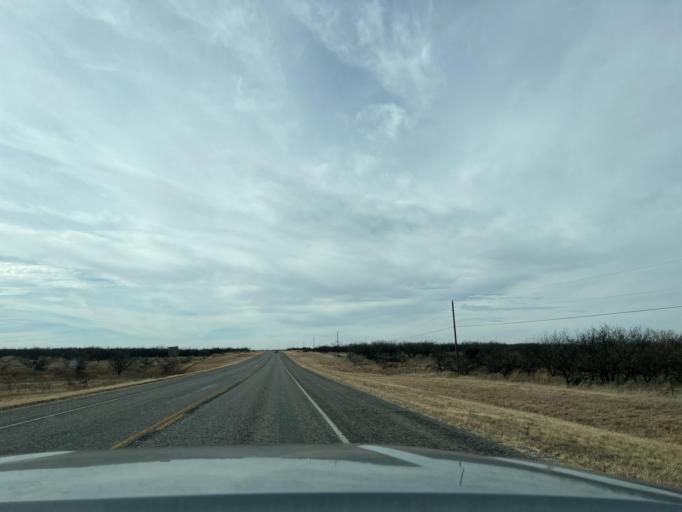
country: US
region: Texas
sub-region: Shackelford County
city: Albany
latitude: 32.7092
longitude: -99.4350
